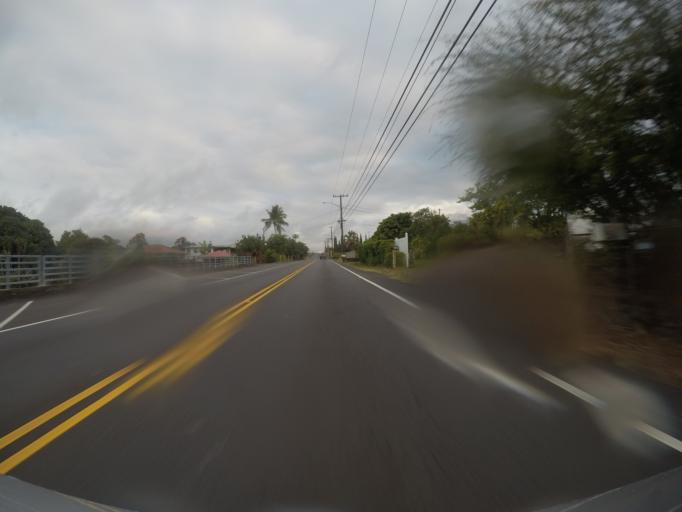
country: US
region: Hawaii
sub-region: Hawaii County
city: Hilo
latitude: 19.6887
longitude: -155.0902
